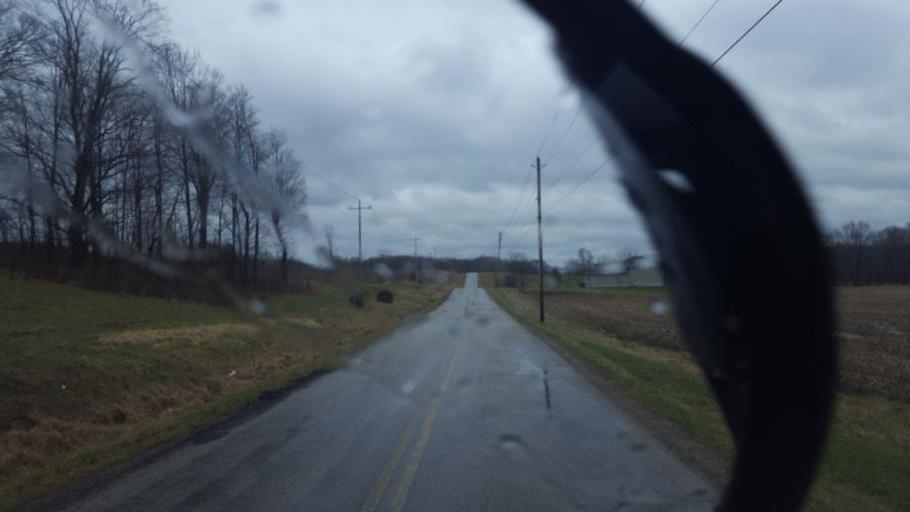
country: US
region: Ohio
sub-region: Sandusky County
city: Bellville
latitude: 40.5593
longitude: -82.5142
